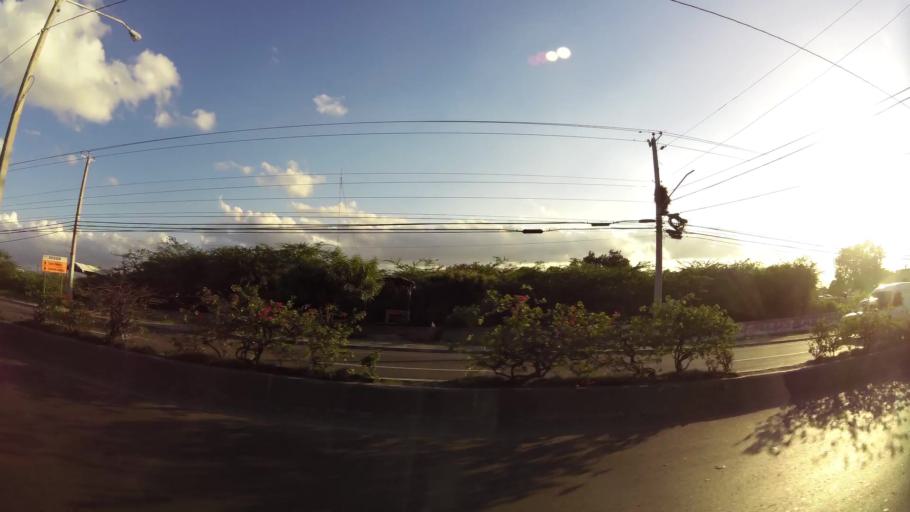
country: DO
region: Santiago
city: Palmar Arriba
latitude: 19.4946
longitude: -70.7318
